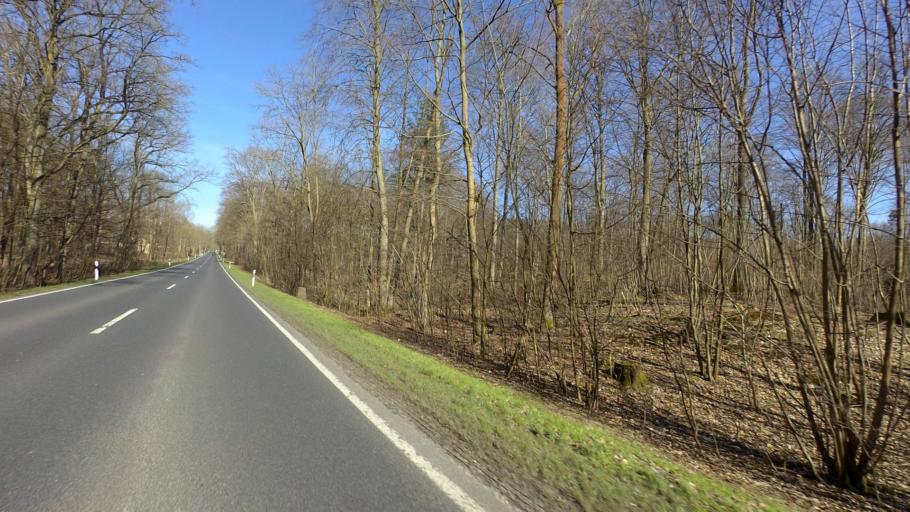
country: DE
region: Brandenburg
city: Eberswalde
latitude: 52.8642
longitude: 13.8380
